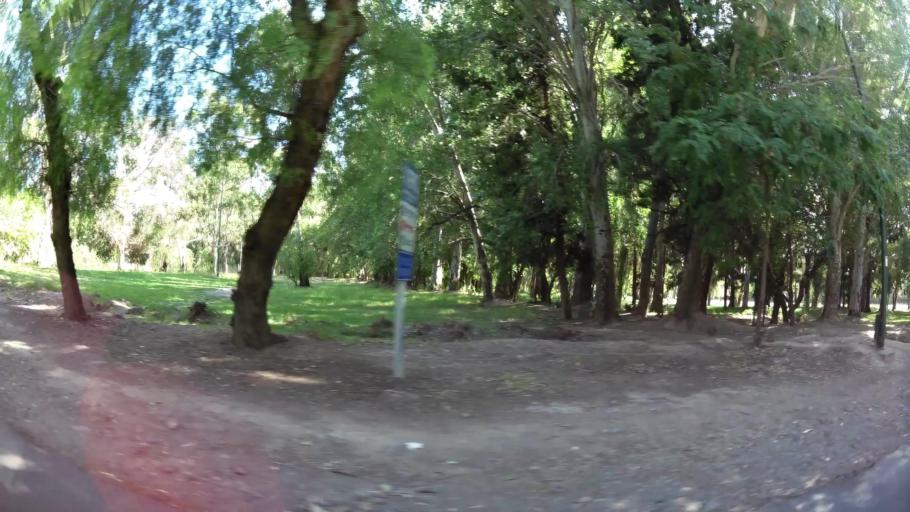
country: AR
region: Mendoza
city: Mendoza
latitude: -32.8929
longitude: -68.8745
